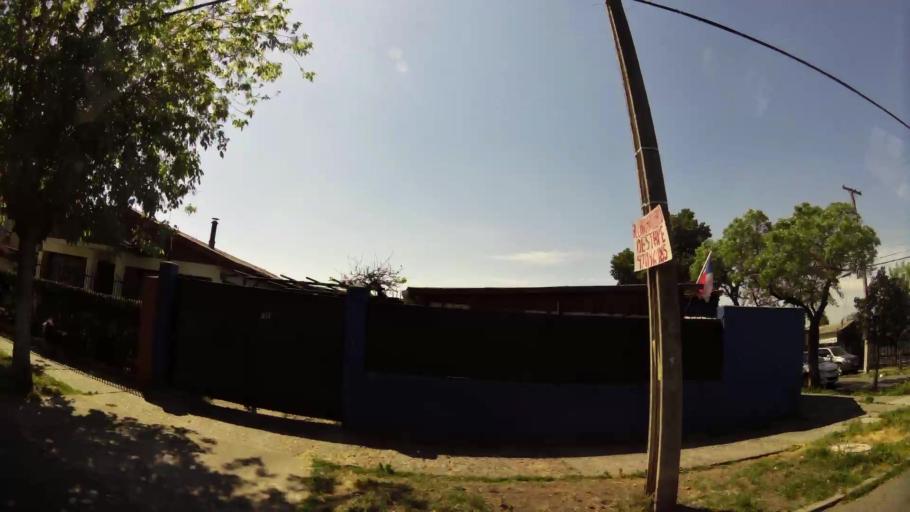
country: CL
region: Santiago Metropolitan
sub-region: Provincia de Santiago
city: Santiago
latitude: -33.5124
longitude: -70.6507
